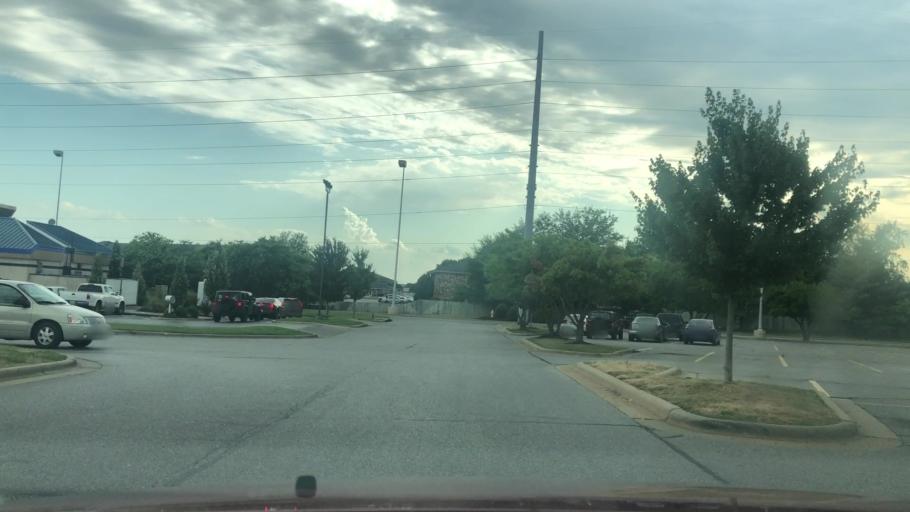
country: US
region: Missouri
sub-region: Greene County
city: Springfield
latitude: 37.1506
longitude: -93.2629
